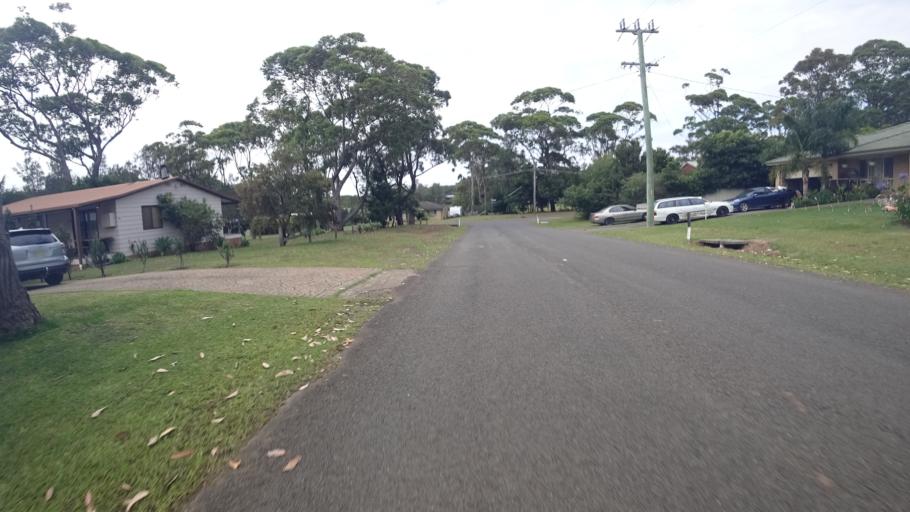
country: AU
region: New South Wales
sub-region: Shoalhaven Shire
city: Milton
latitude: -35.2577
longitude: 150.5131
